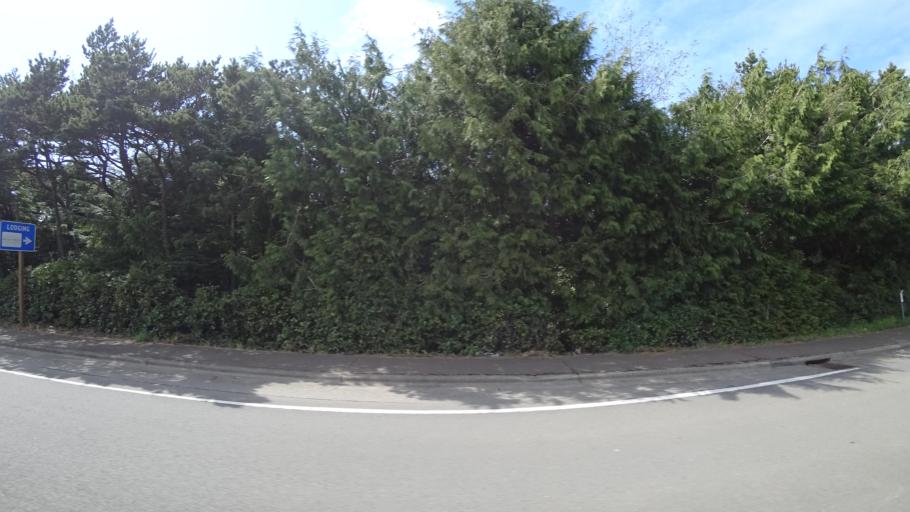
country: US
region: Oregon
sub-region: Lincoln County
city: Lincoln Beach
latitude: 44.8623
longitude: -124.0375
